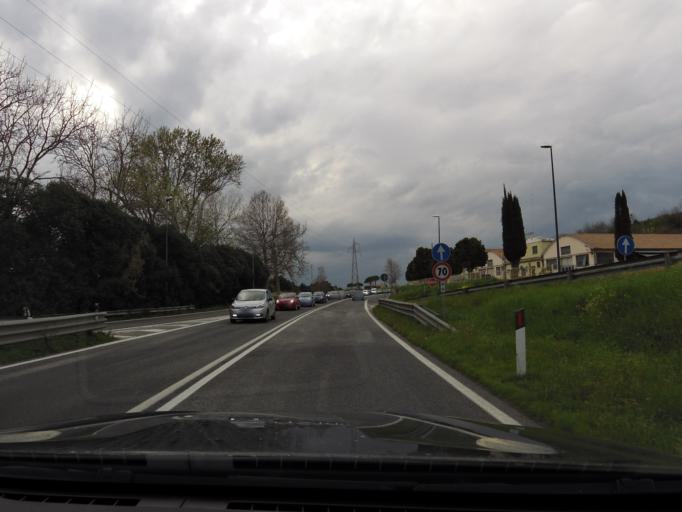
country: IT
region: The Marches
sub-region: Provincia di Ancona
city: Loreto Stazione
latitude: 43.4393
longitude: 13.6391
